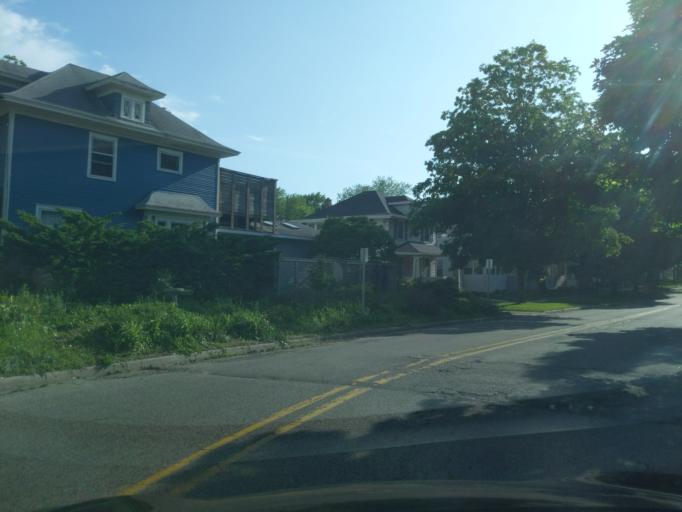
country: US
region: Michigan
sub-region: Ingham County
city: Lansing
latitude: 42.7324
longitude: -84.5331
